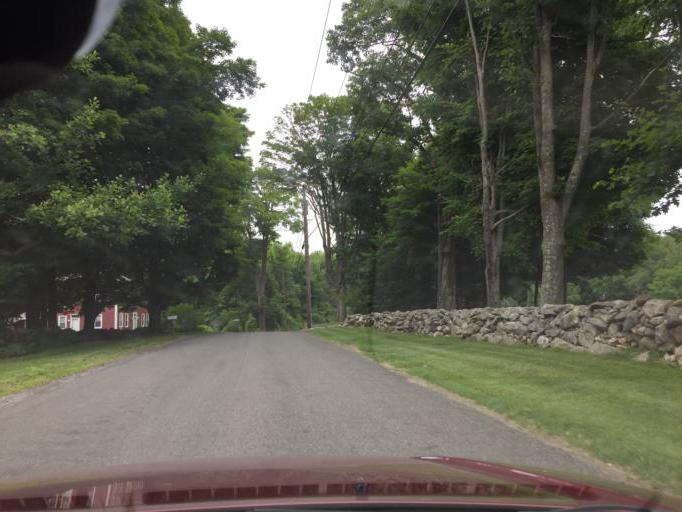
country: US
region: Connecticut
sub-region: Litchfield County
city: Litchfield
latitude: 41.8204
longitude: -73.2623
